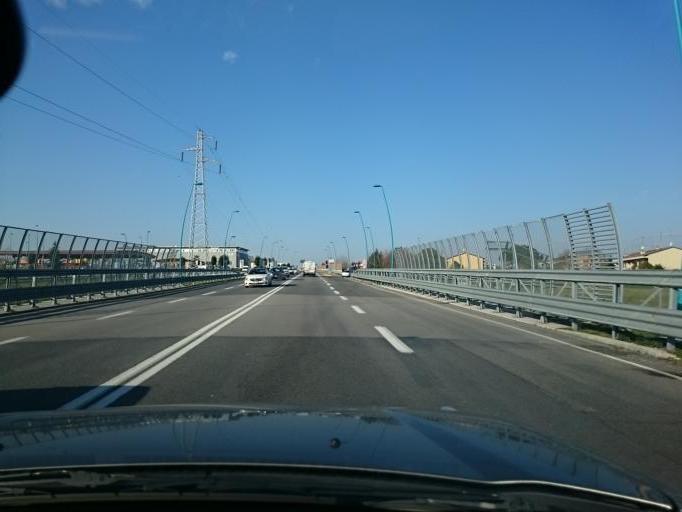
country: IT
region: Veneto
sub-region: Provincia di Verona
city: Peschiera del Garda
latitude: 45.4311
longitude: 10.6971
